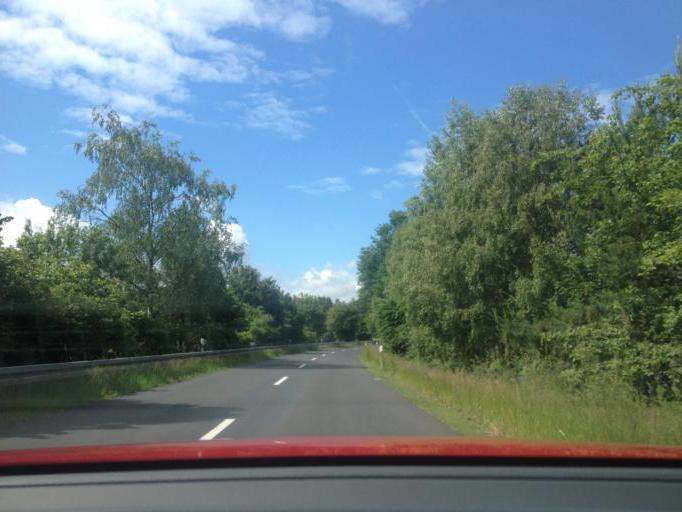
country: DE
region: Bavaria
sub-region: Upper Franconia
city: Arzberg
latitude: 50.0074
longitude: 12.2059
